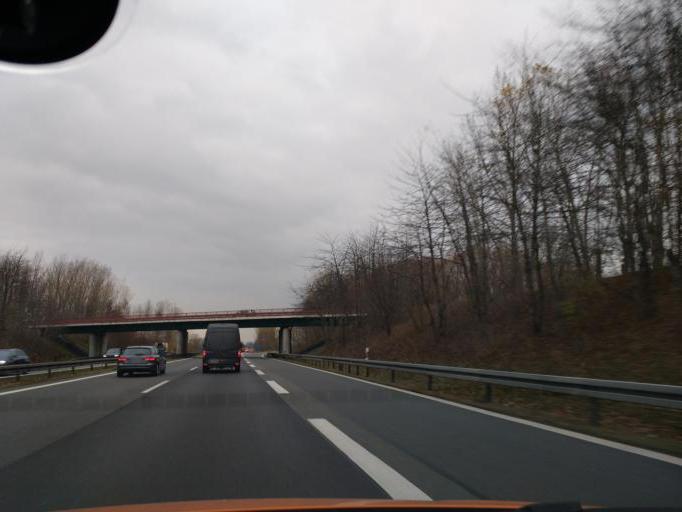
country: DE
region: Brandenburg
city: Fehrbellin
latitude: 52.8020
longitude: 12.7946
